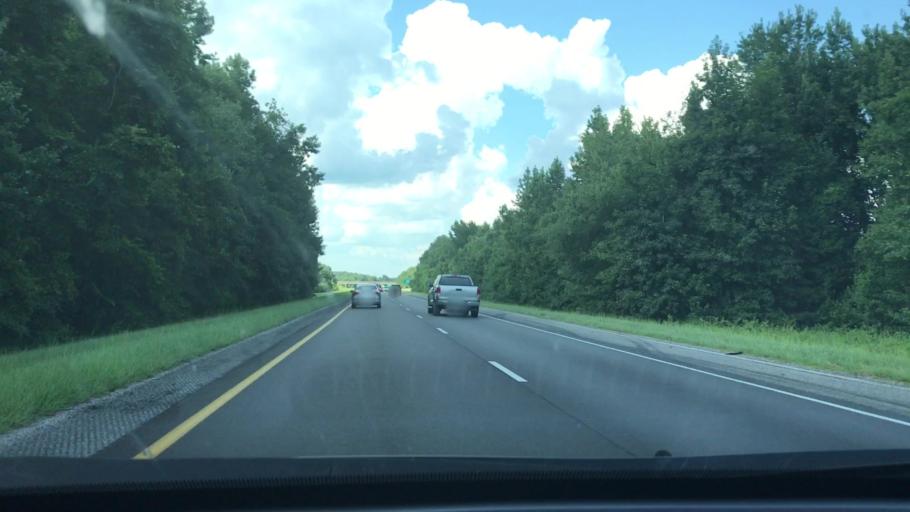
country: US
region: South Carolina
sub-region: Clarendon County
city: Manning
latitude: 33.8530
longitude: -80.1173
